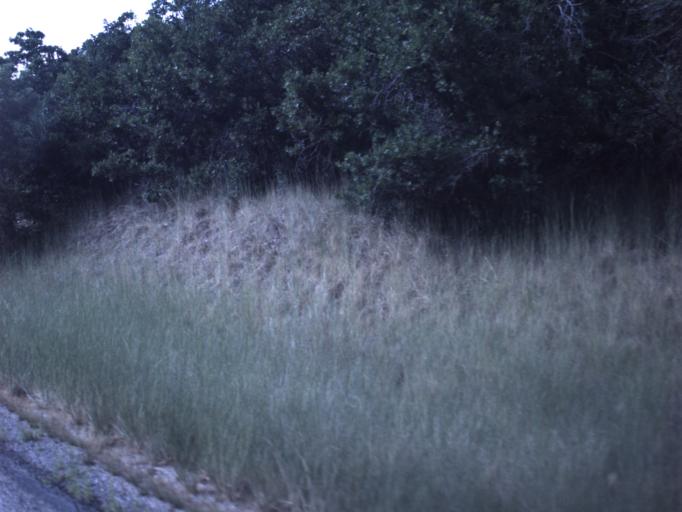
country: US
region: Utah
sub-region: Wasatch County
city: Heber
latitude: 40.4150
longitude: -111.3307
